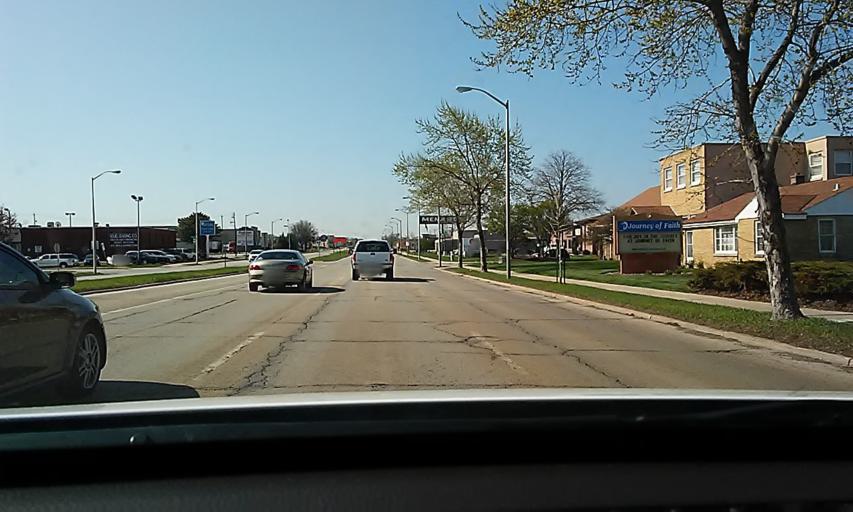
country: US
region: Wisconsin
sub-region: Milwaukee County
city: West Allis
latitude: 42.9994
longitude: -88.0469
